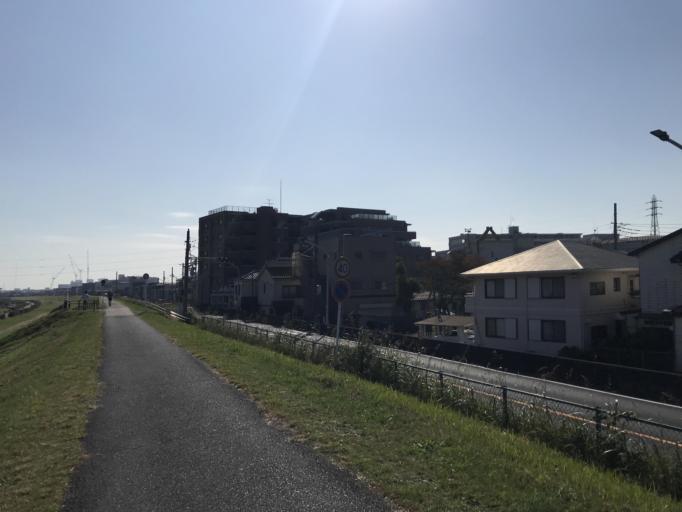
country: JP
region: Kanagawa
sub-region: Kawasaki-shi
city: Kawasaki
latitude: 35.5591
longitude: 139.6814
